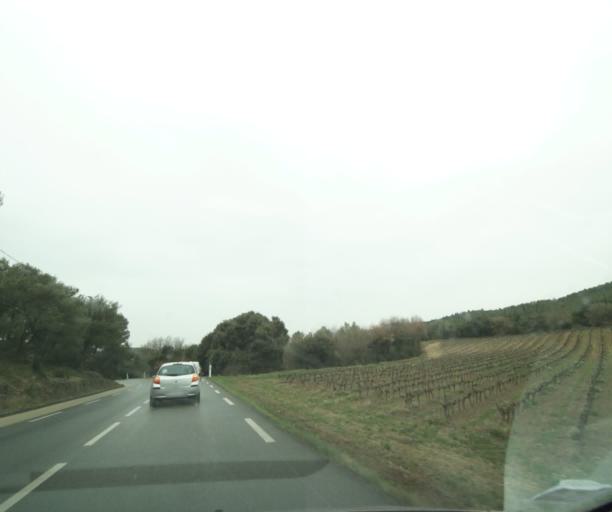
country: FR
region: Provence-Alpes-Cote d'Azur
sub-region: Departement des Bouches-du-Rhone
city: Rognes
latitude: 43.6578
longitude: 5.3630
